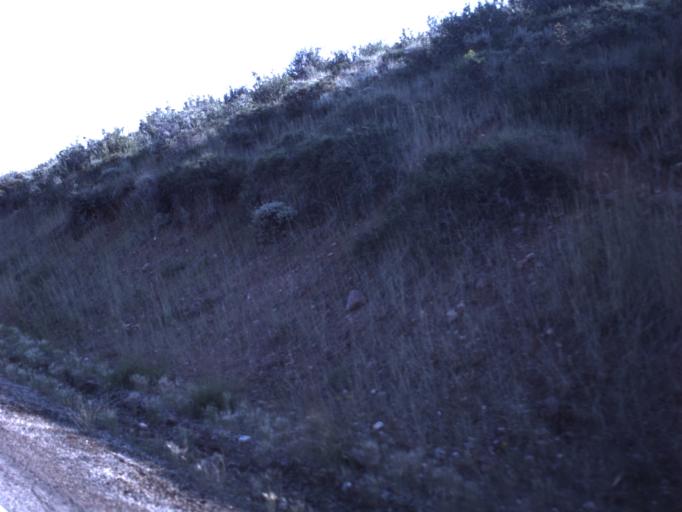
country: US
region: Utah
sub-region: Uintah County
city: Maeser
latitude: 40.6722
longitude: -109.4838
